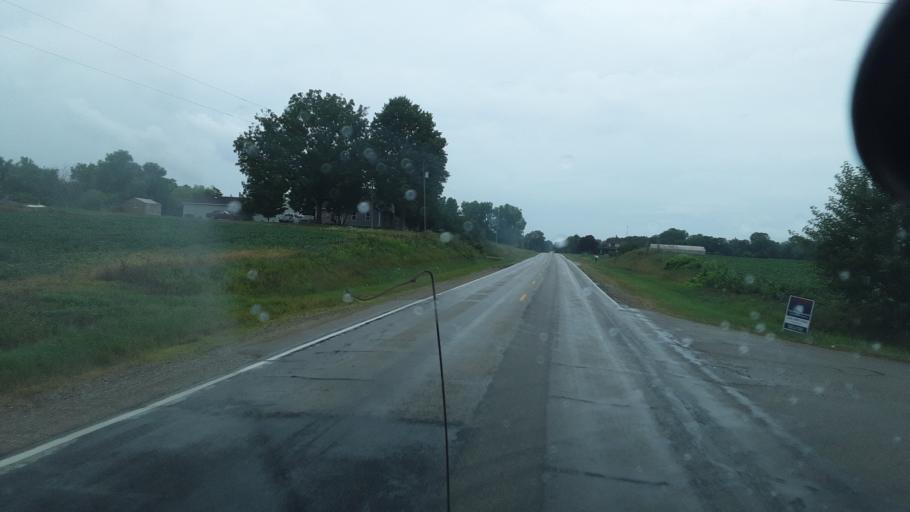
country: US
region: Indiana
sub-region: Steuben County
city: Hamilton
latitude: 41.5591
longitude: -84.8262
